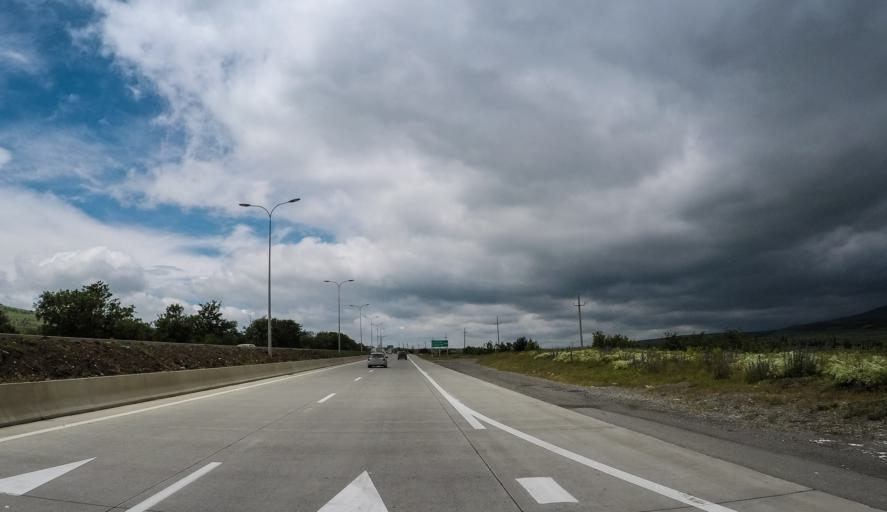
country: GE
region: Shida Kartli
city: Kaspi
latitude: 42.0021
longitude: 44.3782
